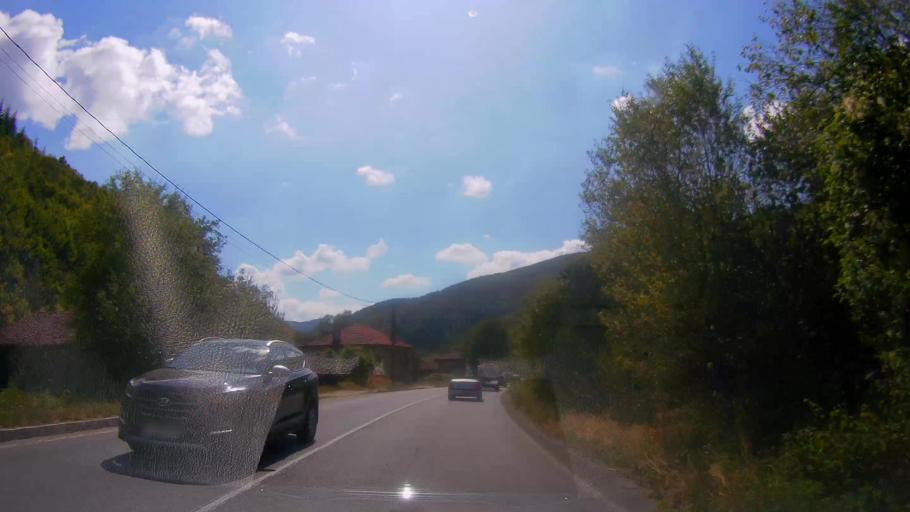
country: BG
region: Stara Zagora
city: Gurkovo
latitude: 42.7420
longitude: 25.7090
